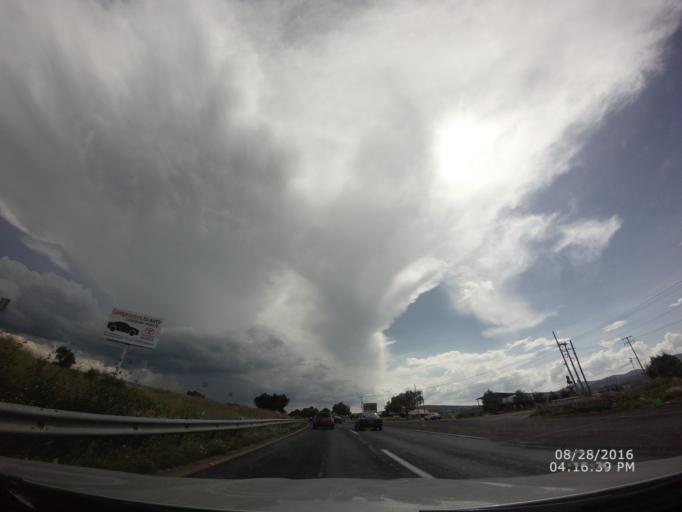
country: MX
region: Hidalgo
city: Zapotlan de Juarez
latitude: 19.9849
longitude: -98.8446
